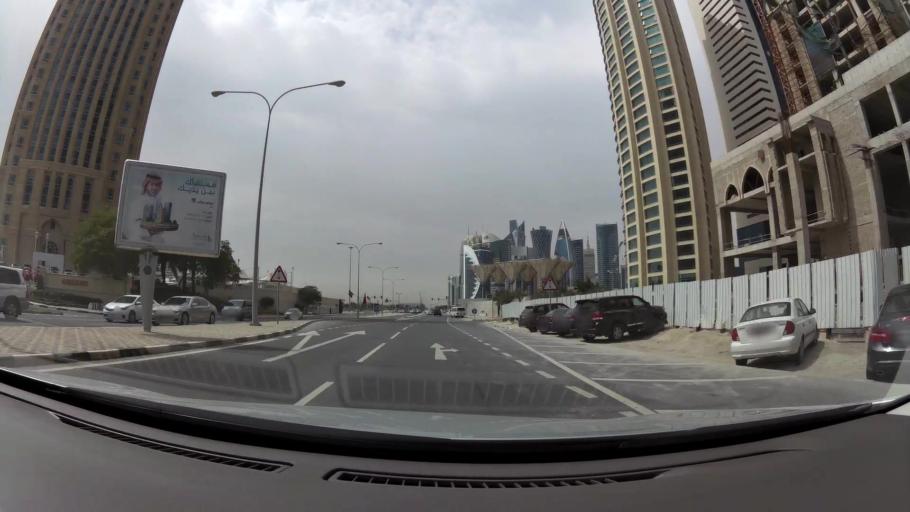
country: QA
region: Baladiyat ad Dawhah
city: Doha
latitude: 25.3243
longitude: 51.5375
